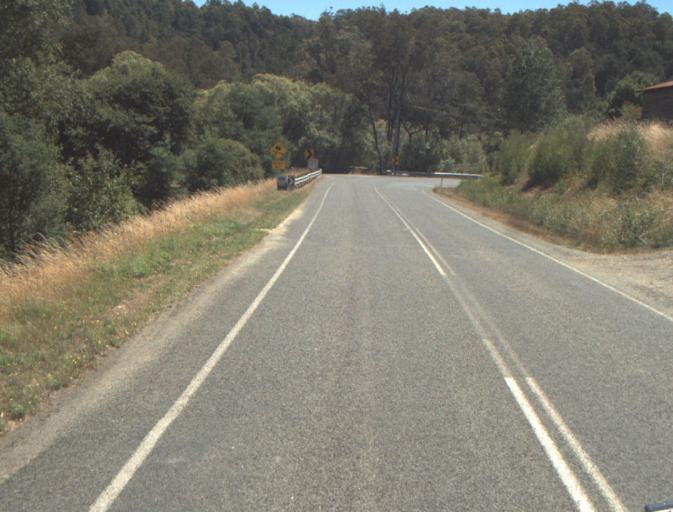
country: AU
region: Tasmania
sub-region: Dorset
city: Scottsdale
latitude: -41.3116
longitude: 147.3680
